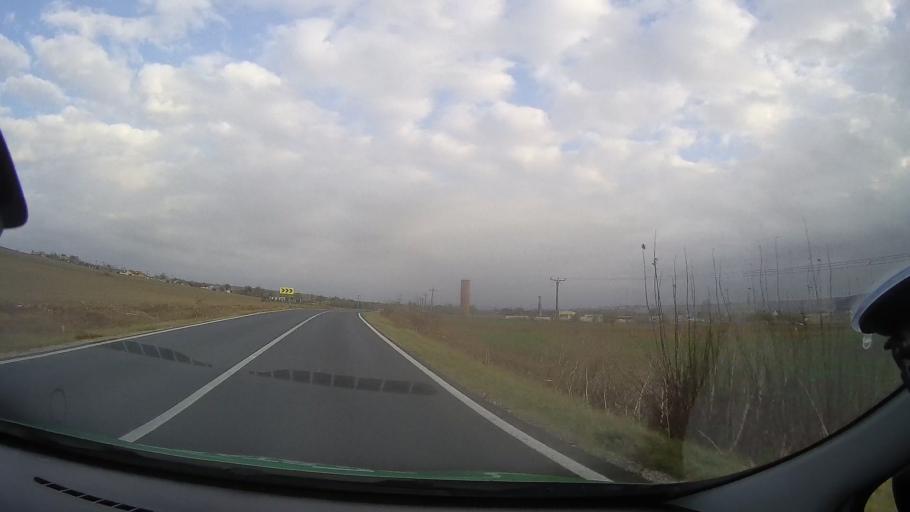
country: RO
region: Constanta
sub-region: Comuna Mircea Voda
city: Satu Nou
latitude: 44.2701
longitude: 28.2123
